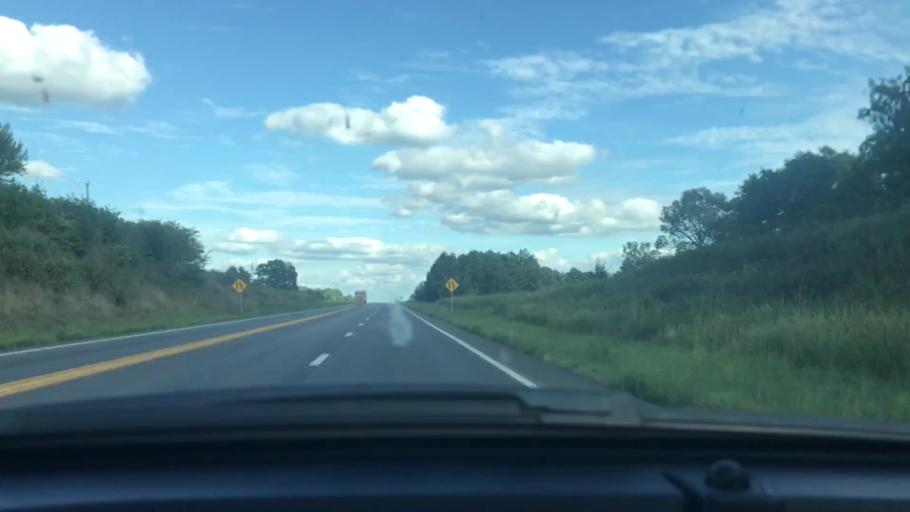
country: US
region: Missouri
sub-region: Oregon County
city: Thayer
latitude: 36.5839
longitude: -91.6143
